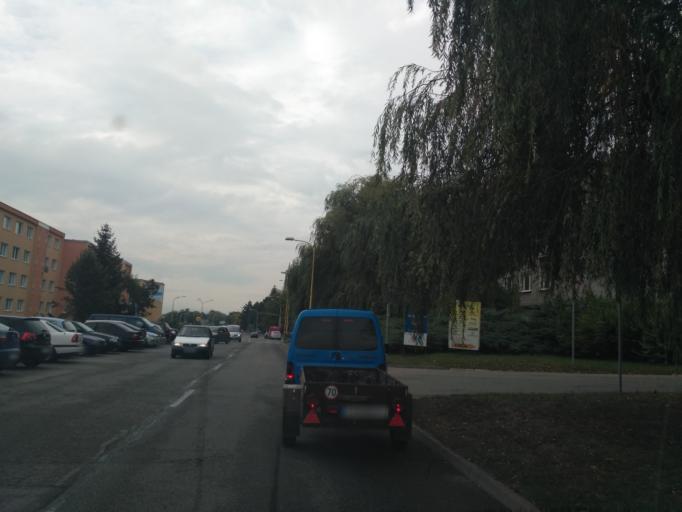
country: SK
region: Kosicky
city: Kosice
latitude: 48.7150
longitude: 21.2265
